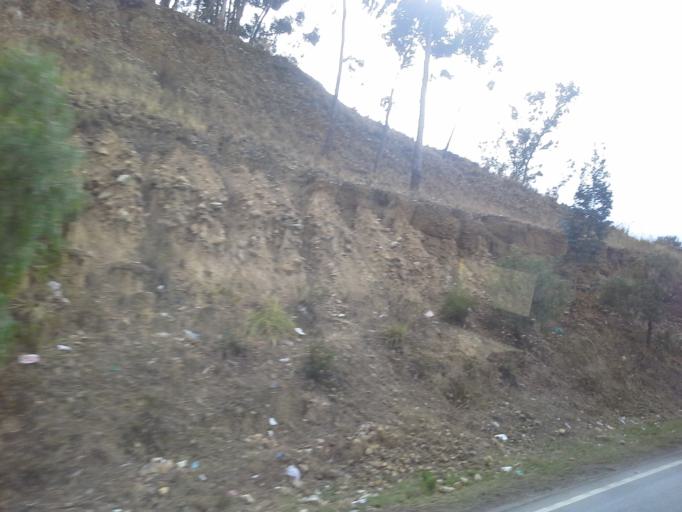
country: BO
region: Cochabamba
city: Colomi
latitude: -17.4136
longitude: -65.9621
